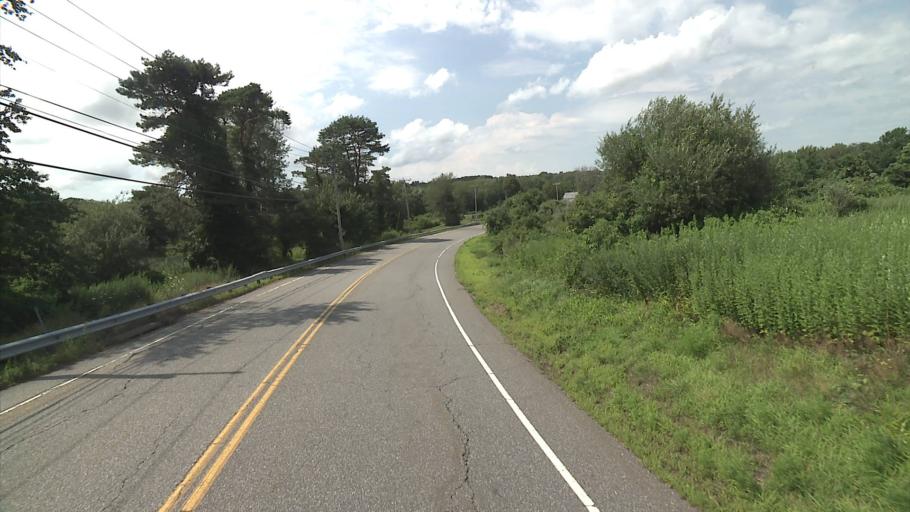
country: US
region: Connecticut
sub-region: New London County
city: Montville Center
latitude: 41.5067
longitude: -72.2457
